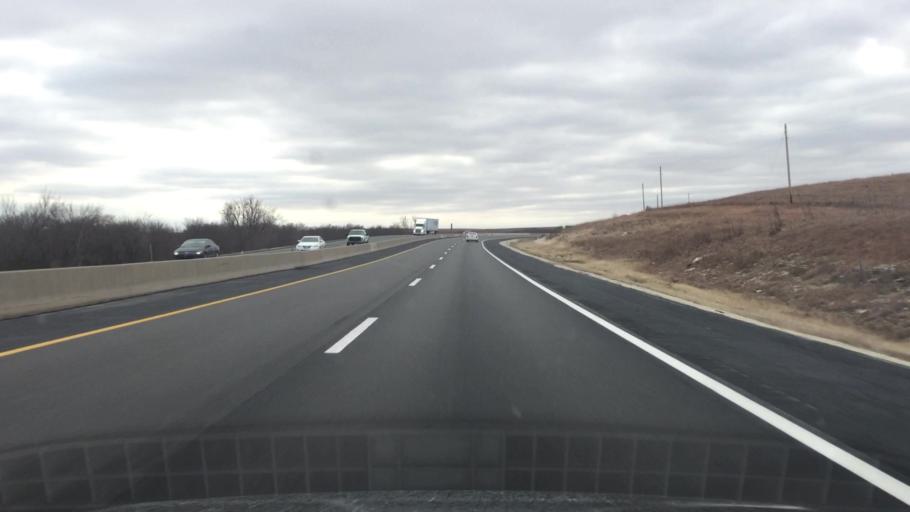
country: US
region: Kansas
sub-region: Chase County
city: Cottonwood Falls
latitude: 38.1523
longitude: -96.4927
